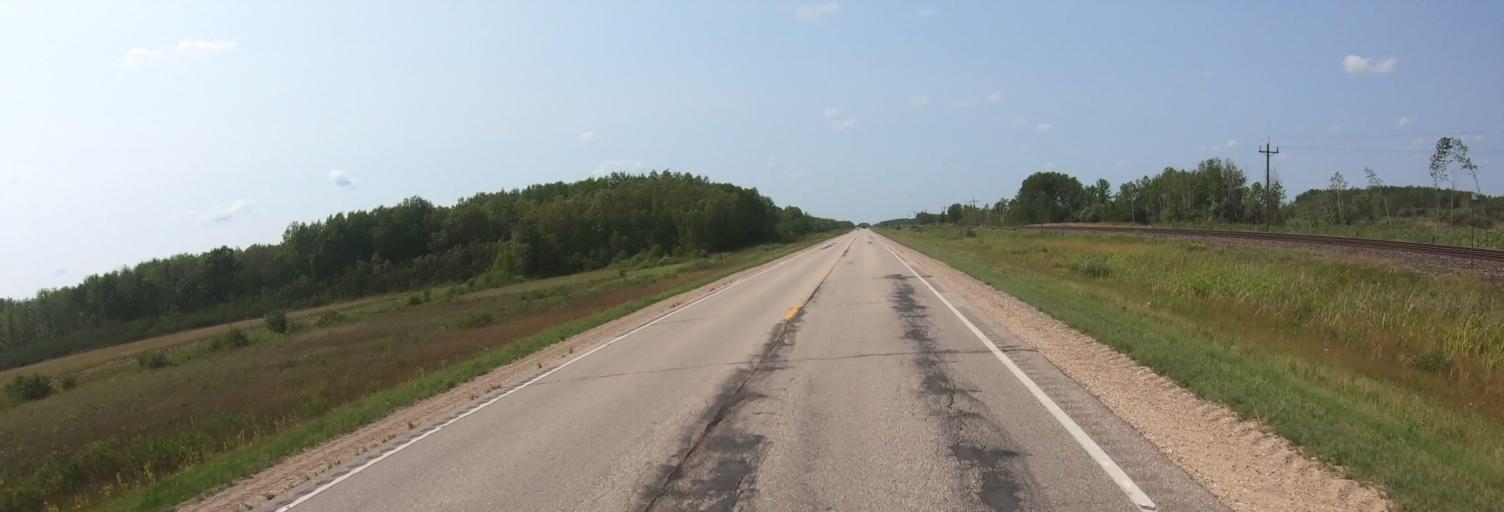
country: US
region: Minnesota
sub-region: Lake of the Woods County
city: Baudette
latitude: 48.7314
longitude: -94.7995
